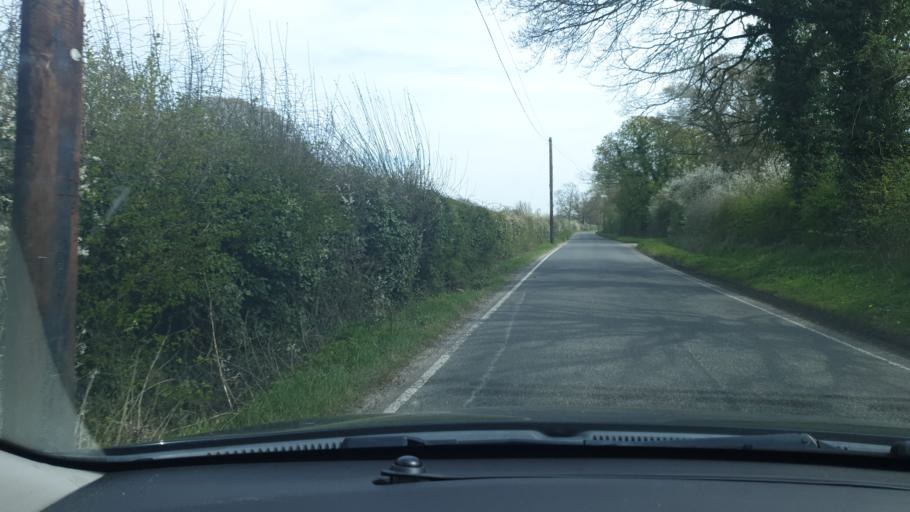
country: GB
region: England
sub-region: Essex
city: Mistley
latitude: 51.9111
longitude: 1.1613
